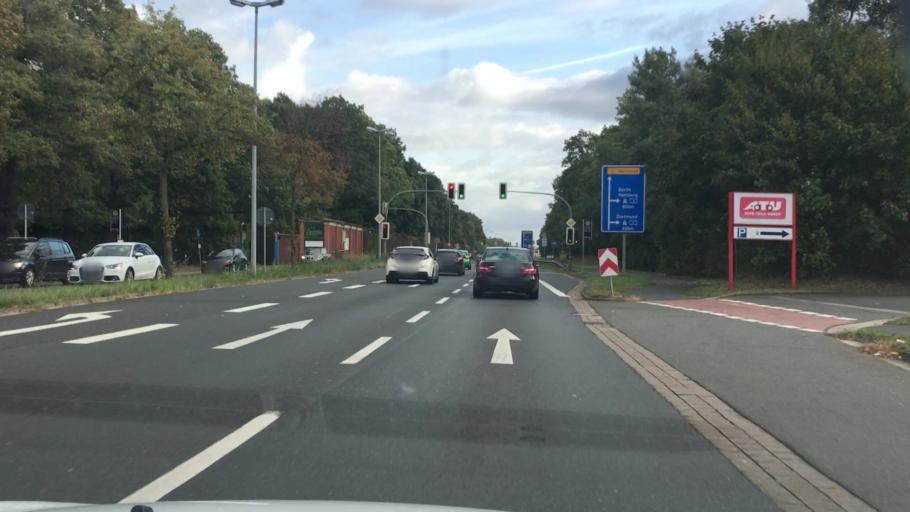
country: DE
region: Lower Saxony
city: Garbsen-Mitte
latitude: 52.4259
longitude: 9.6227
